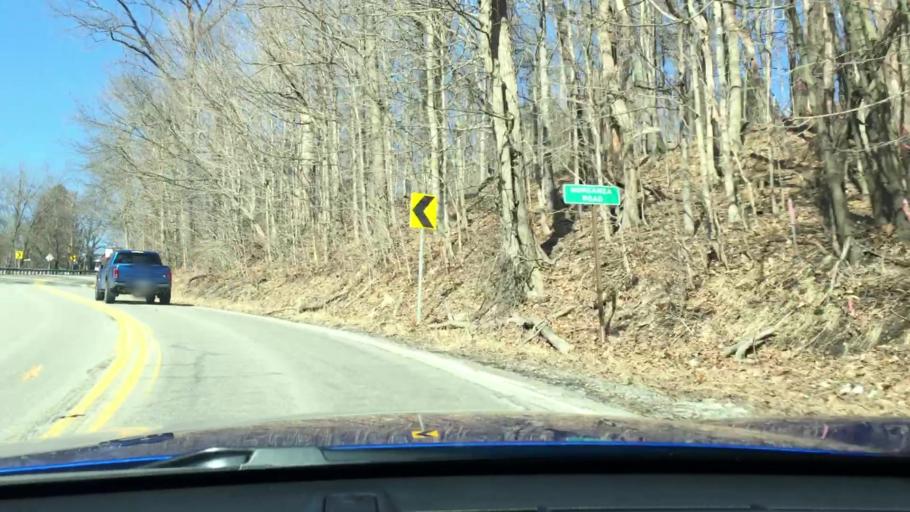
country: US
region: Pennsylvania
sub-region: Washington County
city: Cecil-Bishop
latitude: 40.2999
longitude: -80.1526
